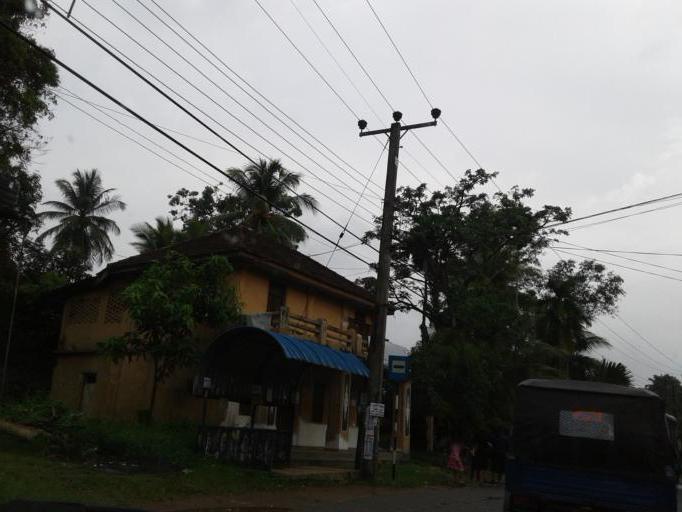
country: LK
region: Central
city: Kadugannawa
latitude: 7.2416
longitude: 80.3221
